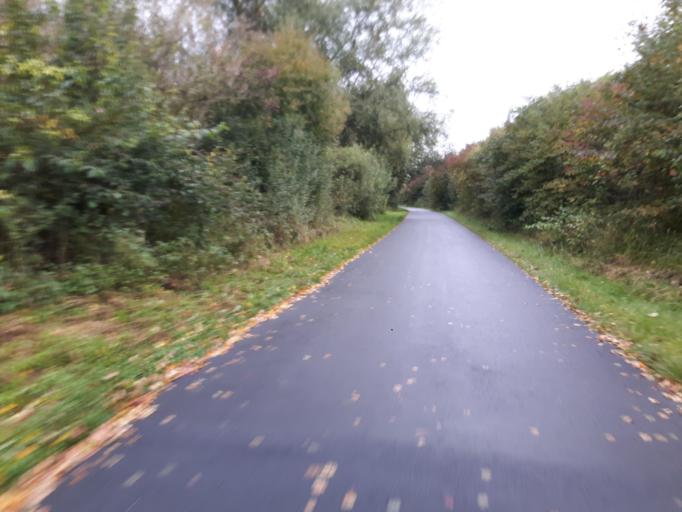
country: DE
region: Bavaria
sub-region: Regierungsbezirk Unterfranken
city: Erlabrunn
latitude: 49.8629
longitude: 9.8418
